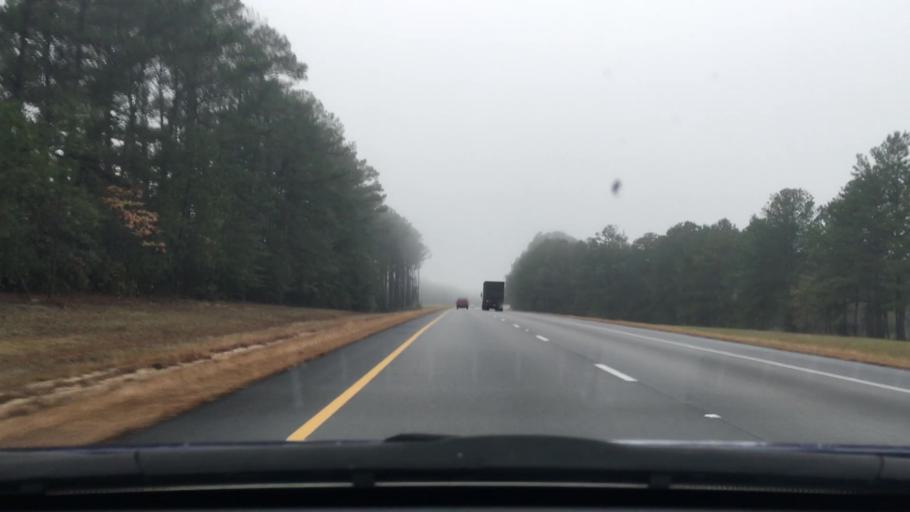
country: US
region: South Carolina
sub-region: Lee County
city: Bishopville
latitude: 34.2043
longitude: -80.3787
